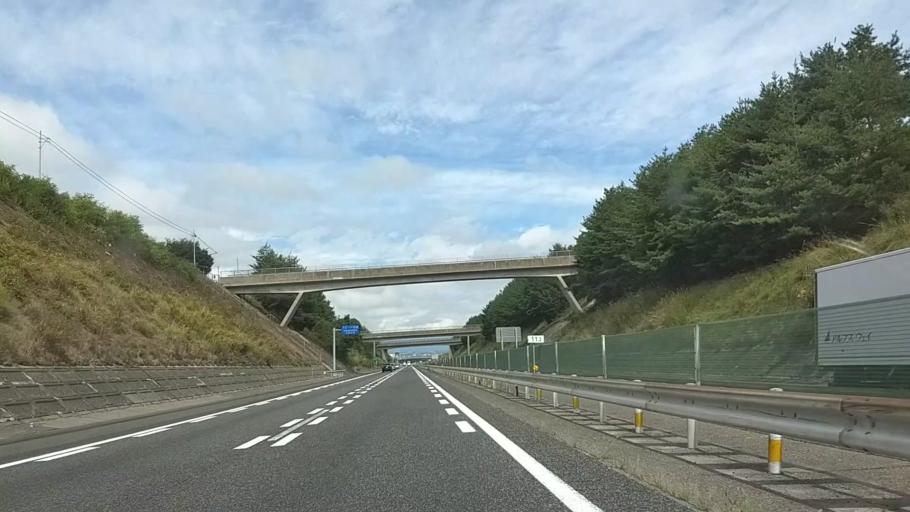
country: JP
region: Nagano
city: Shiojiri
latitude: 36.1215
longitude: 137.9795
